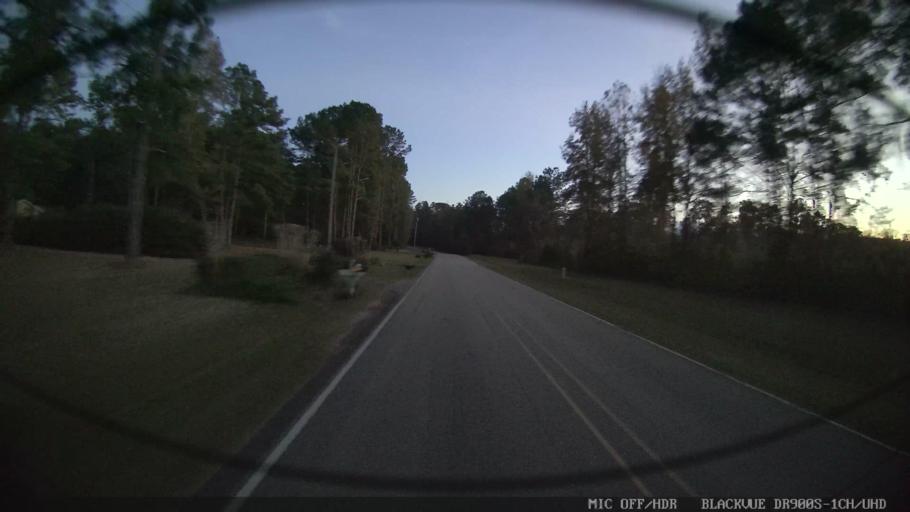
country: US
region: Mississippi
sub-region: Perry County
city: New Augusta
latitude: 31.1577
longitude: -89.2111
